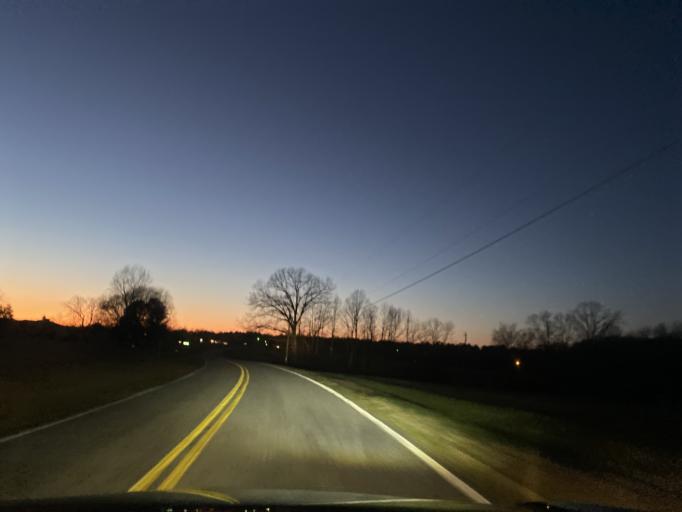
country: US
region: South Carolina
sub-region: Cherokee County
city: Gaffney
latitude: 35.1349
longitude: -81.7137
